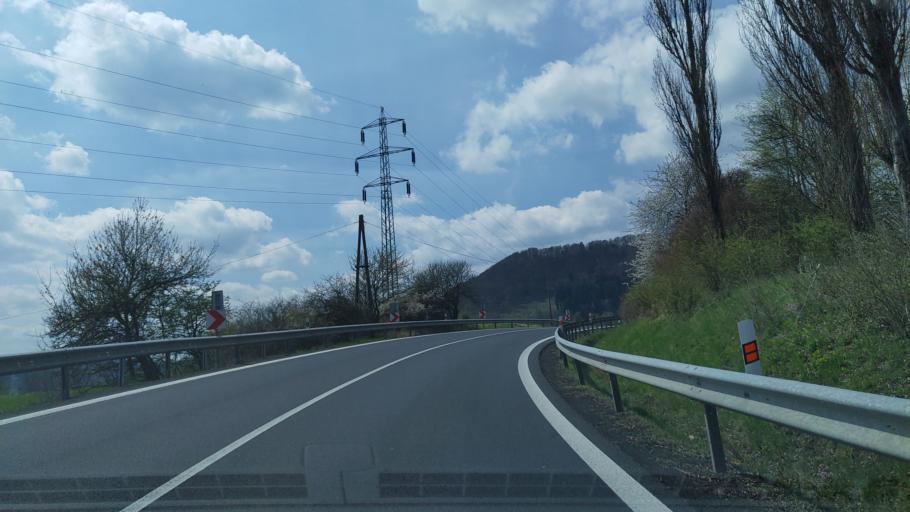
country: CZ
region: Karlovarsky
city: Ostrov
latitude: 50.3317
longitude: 13.0273
